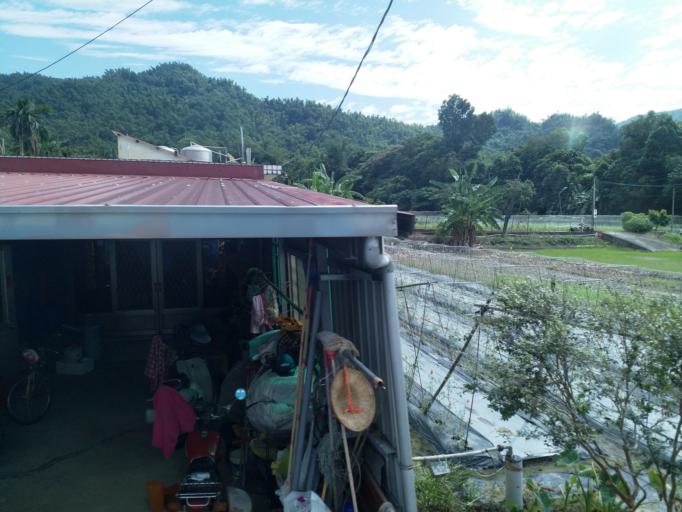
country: TW
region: Taiwan
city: Yujing
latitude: 22.9239
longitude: 120.5840
